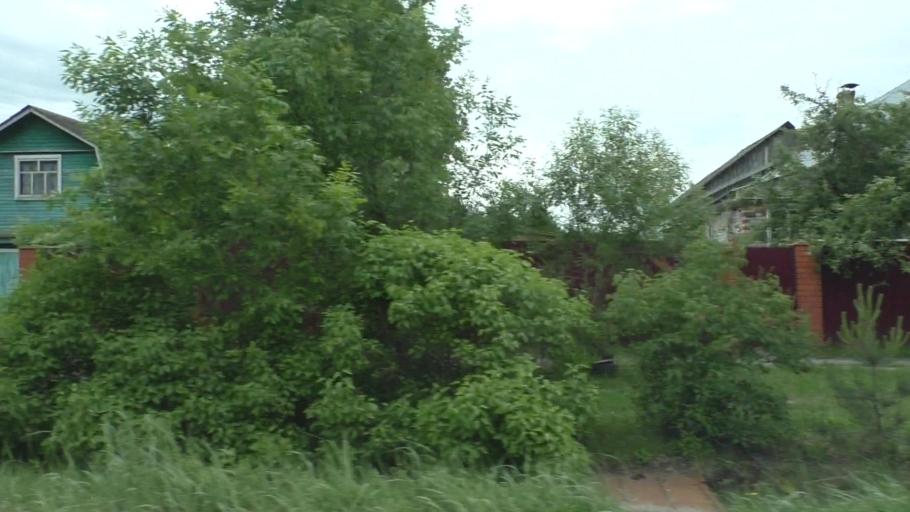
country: RU
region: Moskovskaya
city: Il'inskiy Pogost
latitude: 55.5016
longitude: 38.7972
